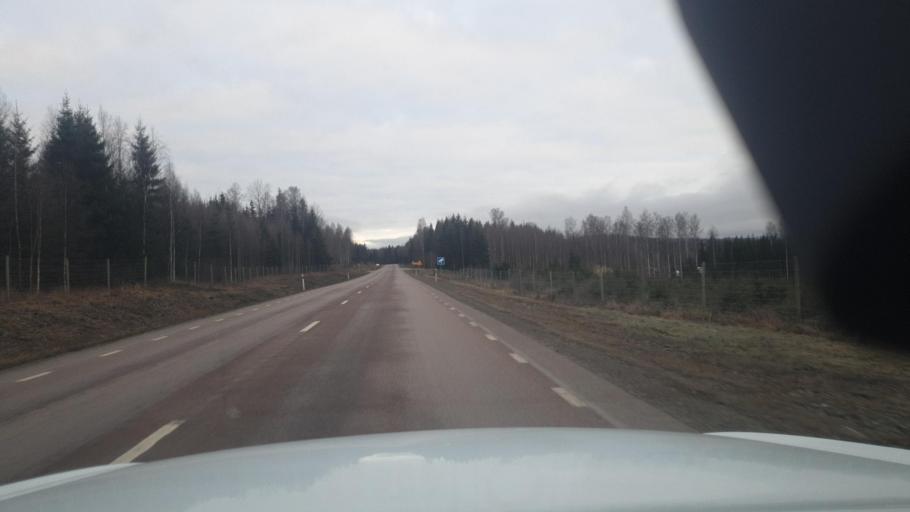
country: SE
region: Vaermland
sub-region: Sunne Kommun
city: Sunne
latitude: 59.7583
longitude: 13.1157
